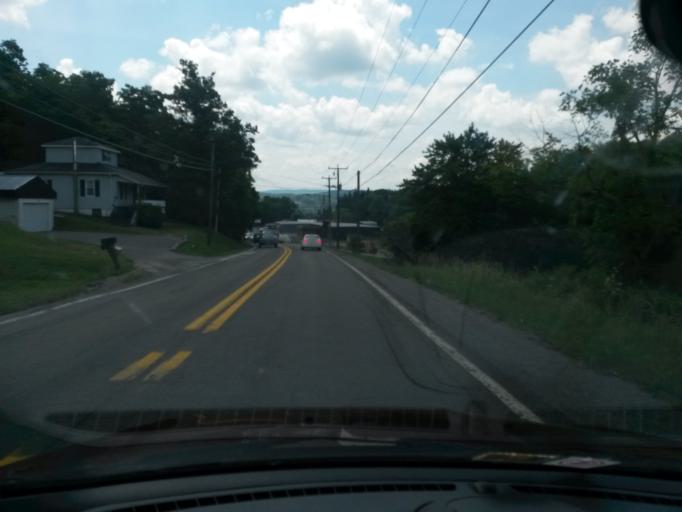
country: US
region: West Virginia
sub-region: Mercer County
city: Princeton
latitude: 37.3725
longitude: -81.1119
